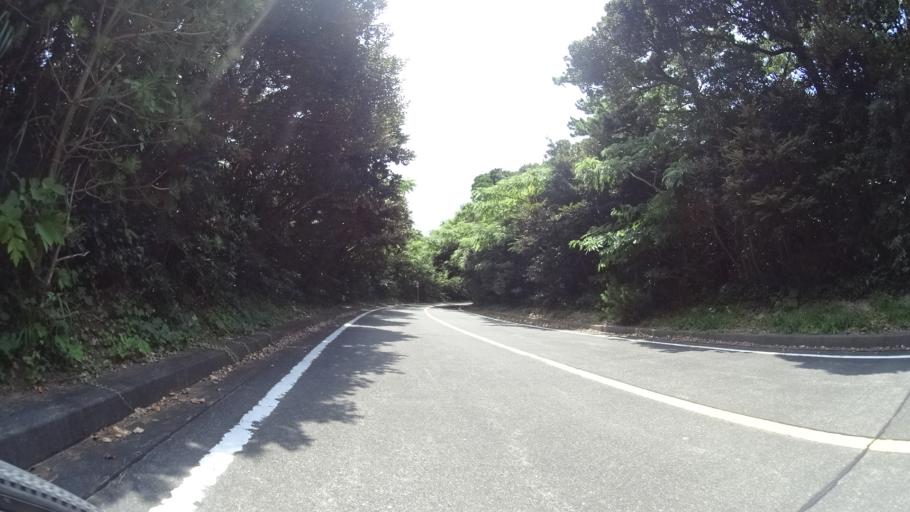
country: JP
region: Shizuoka
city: Shimoda
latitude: 34.3289
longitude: 139.2108
